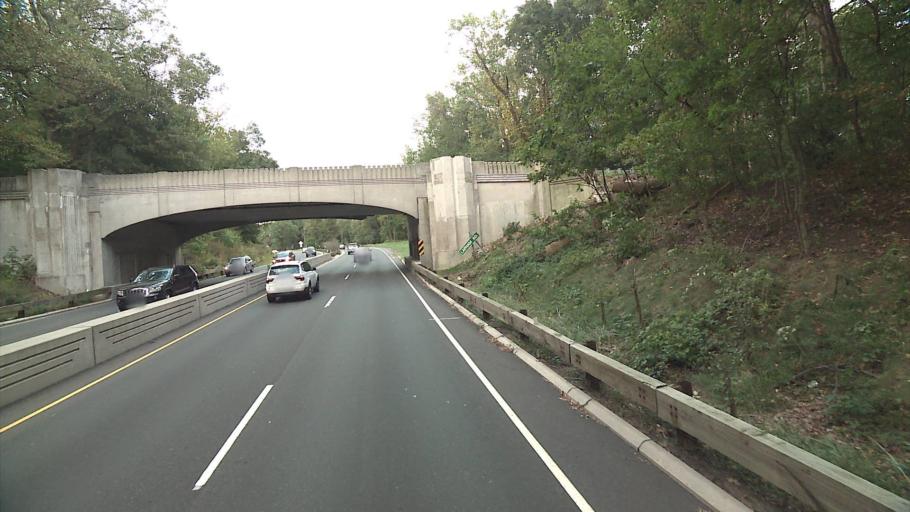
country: US
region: Connecticut
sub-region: Fairfield County
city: New Canaan
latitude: 41.1165
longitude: -73.4940
